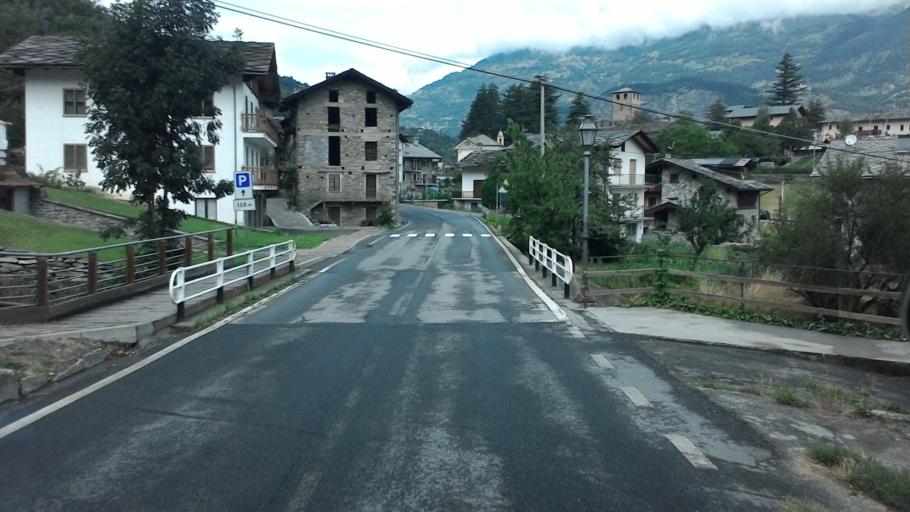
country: IT
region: Aosta Valley
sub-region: Valle d'Aosta
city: Plan d'Introd
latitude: 45.6894
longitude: 7.1886
